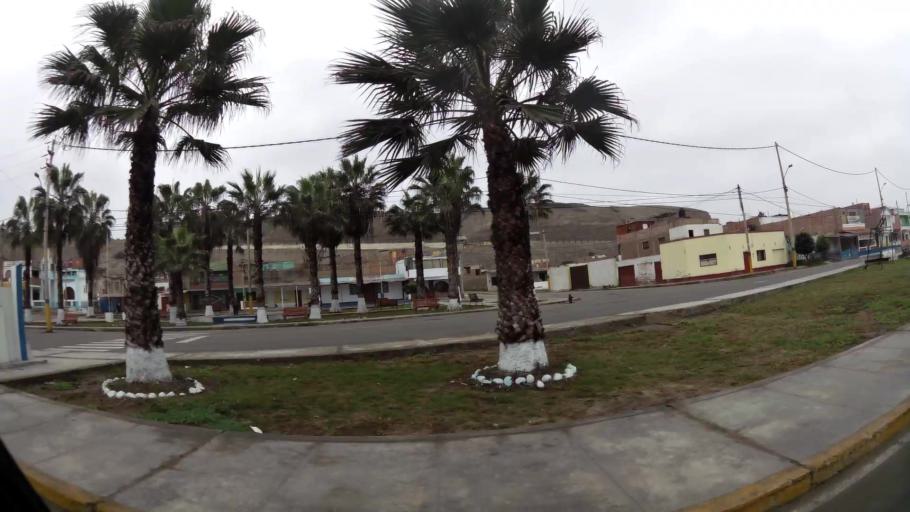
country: PE
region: Lima
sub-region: Barranca
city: Barranca
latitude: -10.7650
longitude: -77.7614
